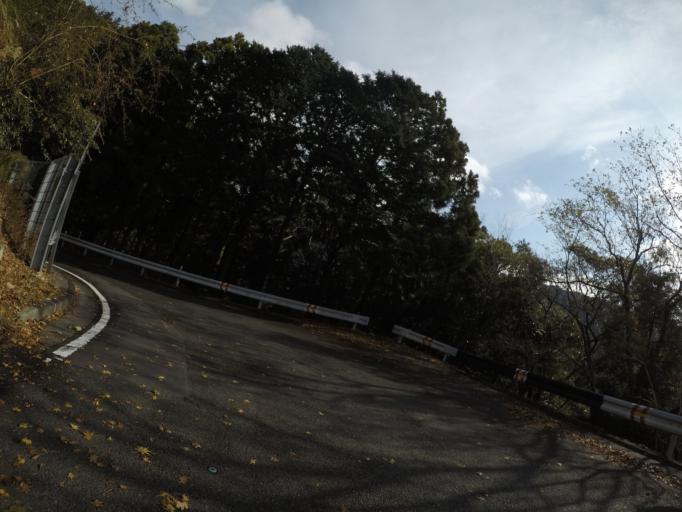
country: JP
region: Shizuoka
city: Heda
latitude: 34.8315
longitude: 138.8528
